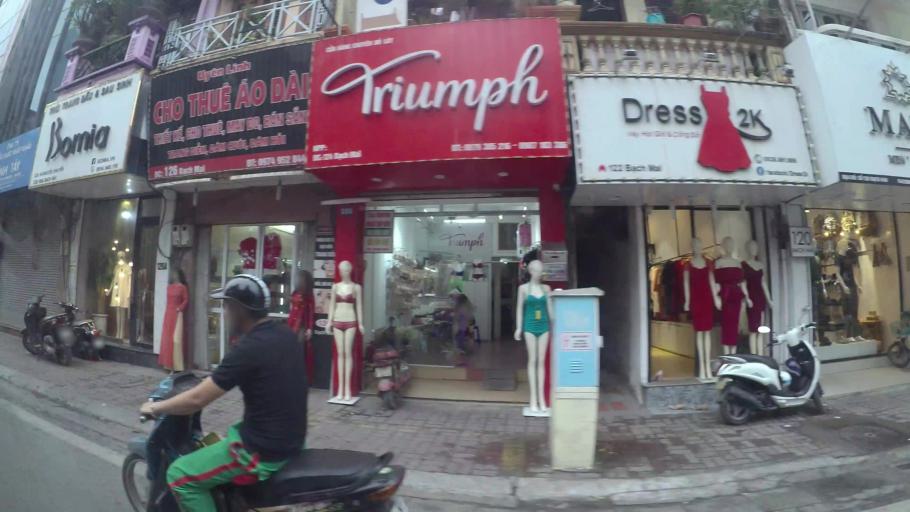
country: VN
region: Ha Noi
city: Hai BaTrung
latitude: 21.0060
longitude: 105.8512
